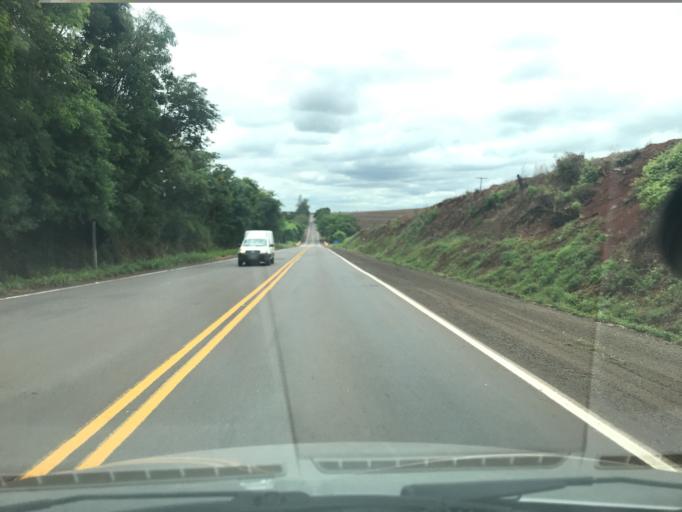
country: BR
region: Parana
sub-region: Terra Boa
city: Terra Boa
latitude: -23.5990
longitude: -52.3952
